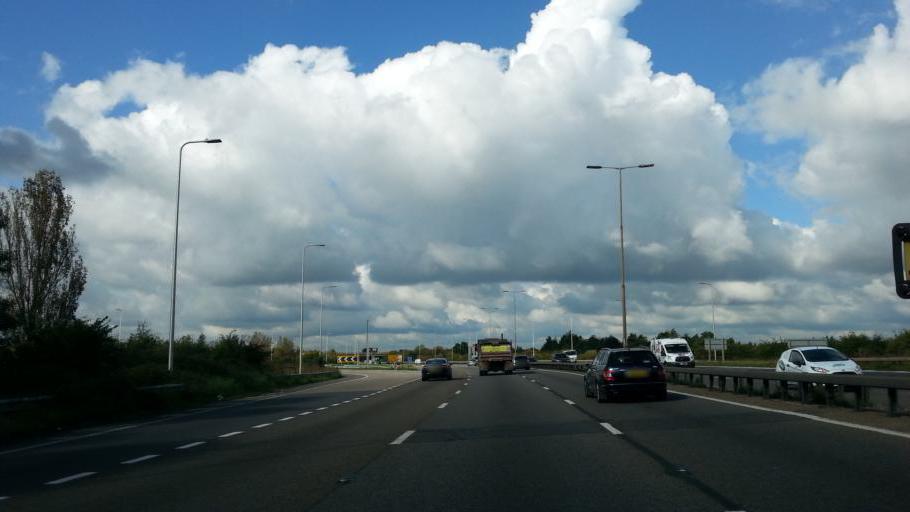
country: GB
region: England
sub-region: Royal Borough of Windsor and Maidenhead
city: Bray
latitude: 51.5115
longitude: -0.6557
